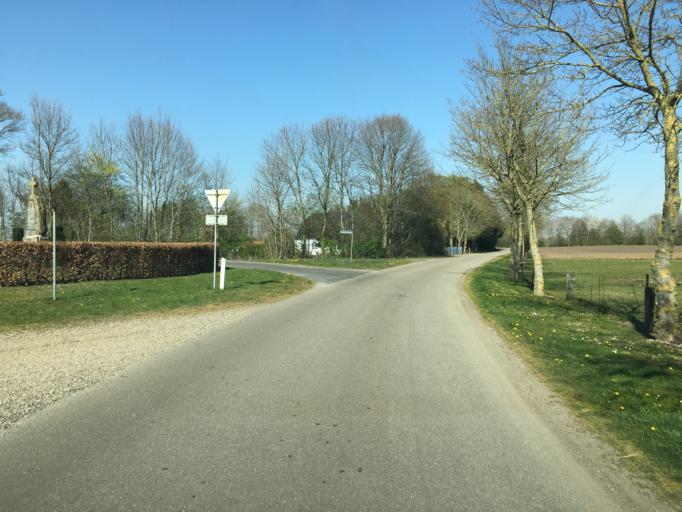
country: DK
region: South Denmark
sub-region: Aabenraa Kommune
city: Rodekro
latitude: 55.0763
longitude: 9.2542
